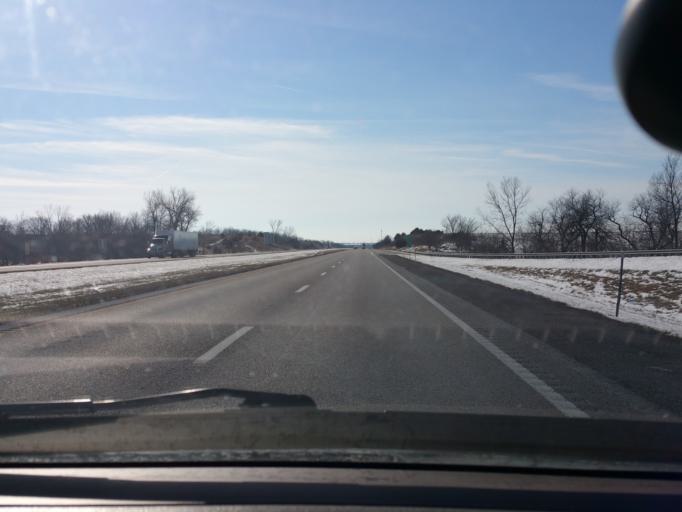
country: US
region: Missouri
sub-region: Clinton County
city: Cameron
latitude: 39.8985
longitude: -94.1522
